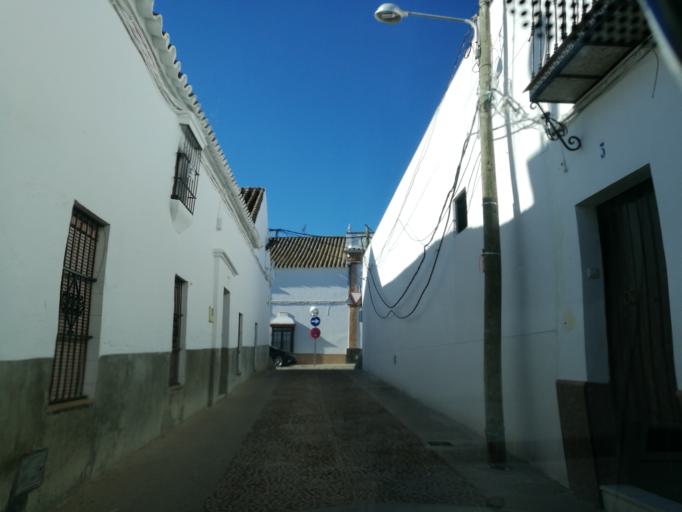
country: ES
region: Andalusia
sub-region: Provincia de Sevilla
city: La Campana
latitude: 37.5683
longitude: -5.4259
